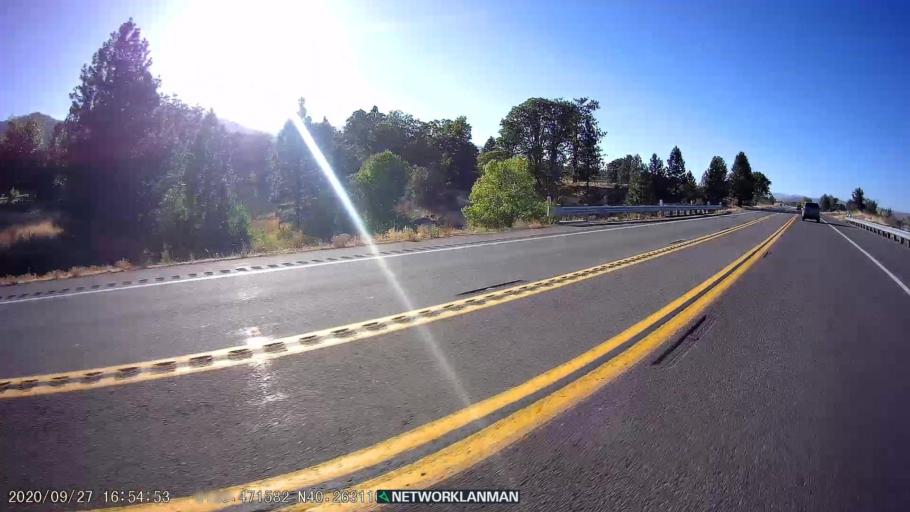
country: US
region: California
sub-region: Lassen County
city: Janesville
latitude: 40.2634
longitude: -120.4718
